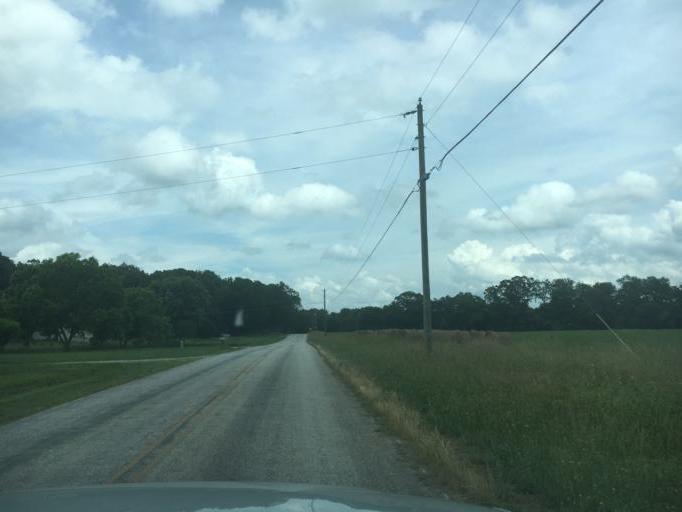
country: US
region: Georgia
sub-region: Hart County
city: Reed Creek
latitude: 34.4281
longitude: -82.9430
